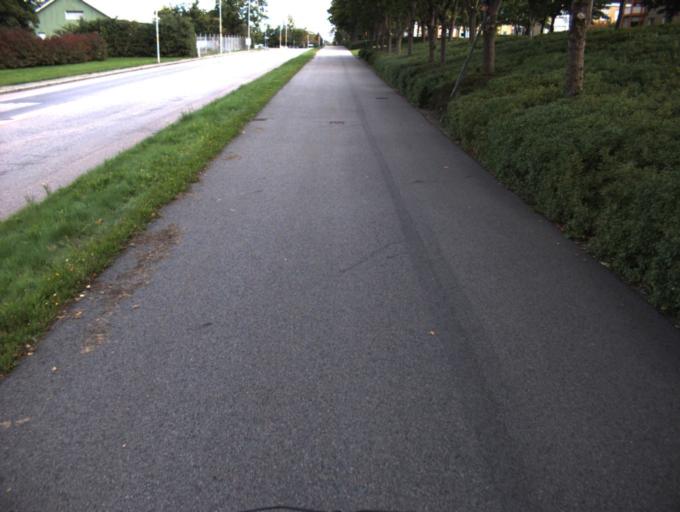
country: SE
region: Skane
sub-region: Helsingborg
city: Helsingborg
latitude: 56.0427
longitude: 12.7453
